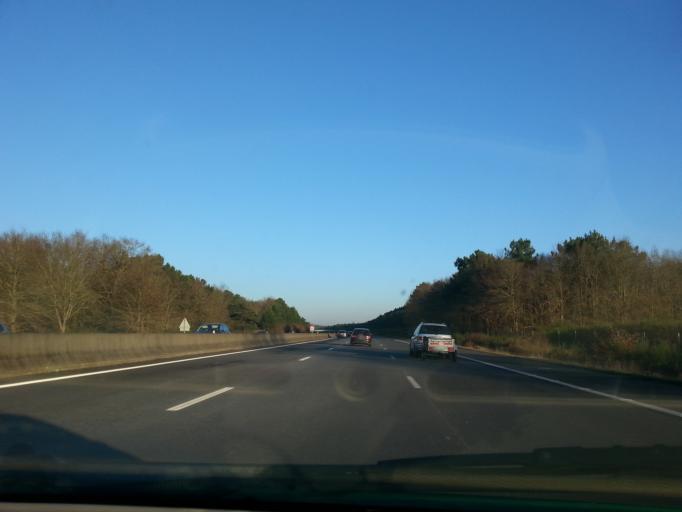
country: FR
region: Pays de la Loire
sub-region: Departement de la Sarthe
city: Saint-Mars-la-Briere
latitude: 48.0552
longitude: 0.3671
